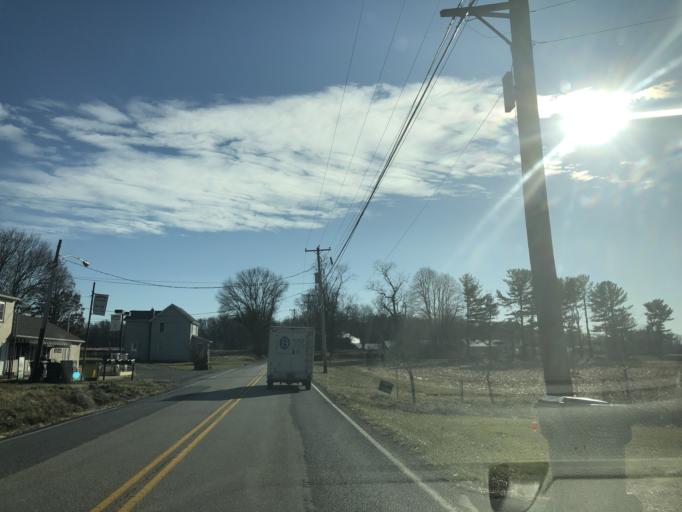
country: US
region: Pennsylvania
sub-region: Chester County
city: Upland
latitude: 39.8670
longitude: -75.7726
